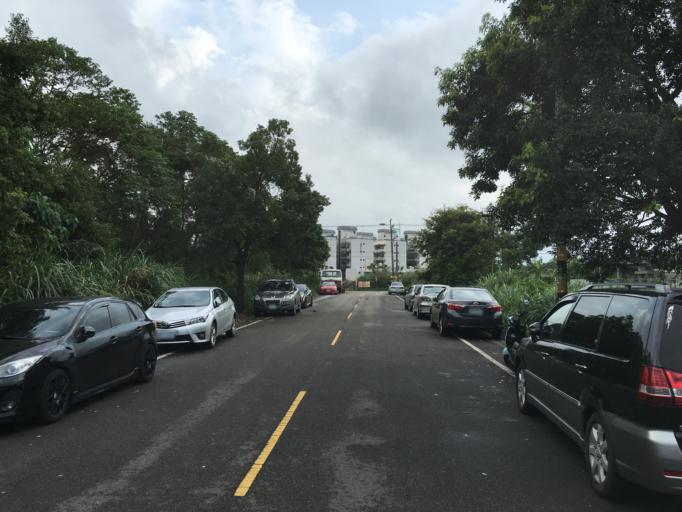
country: TW
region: Taiwan
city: Daxi
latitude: 24.8696
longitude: 121.2310
